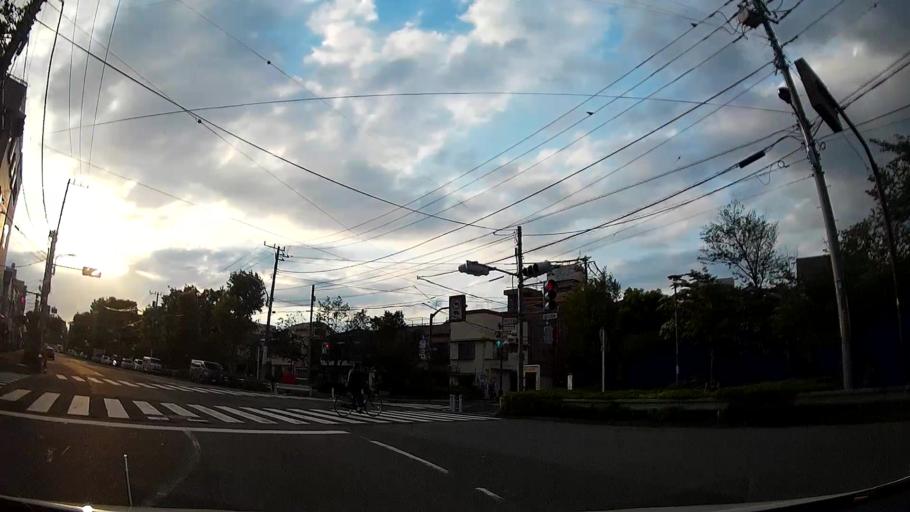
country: JP
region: Saitama
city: Kawaguchi
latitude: 35.7588
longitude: 139.7437
